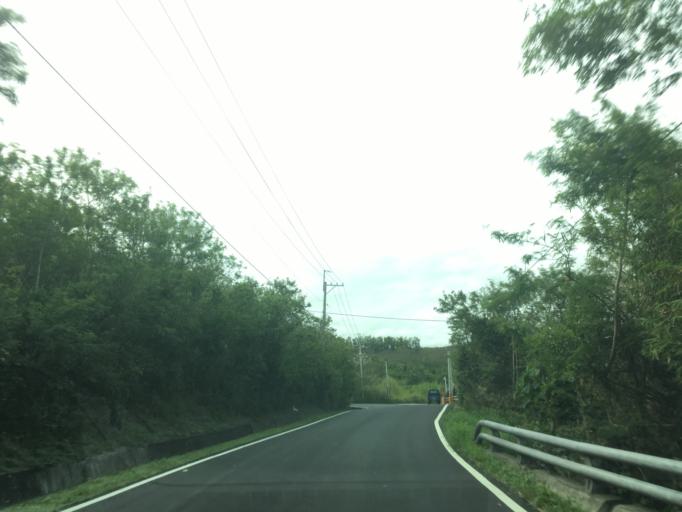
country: TW
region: Taiwan
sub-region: Taitung
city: Taitung
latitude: 22.7909
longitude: 121.1618
